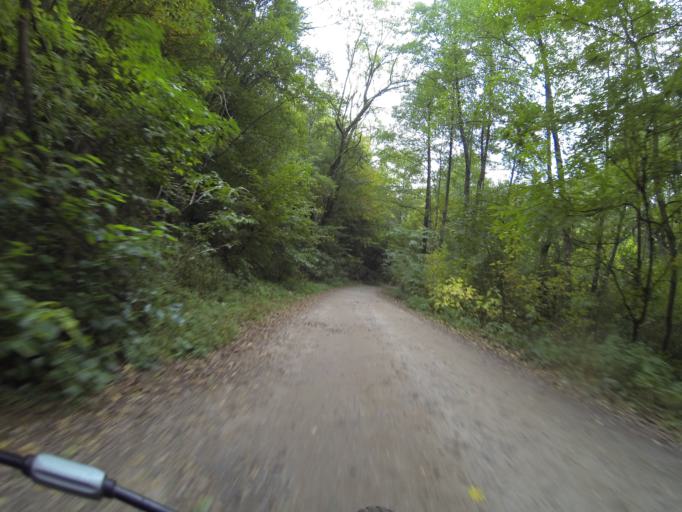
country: RO
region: Gorj
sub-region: Comuna Tismana
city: Pocruia
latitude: 45.0529
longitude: 22.9145
